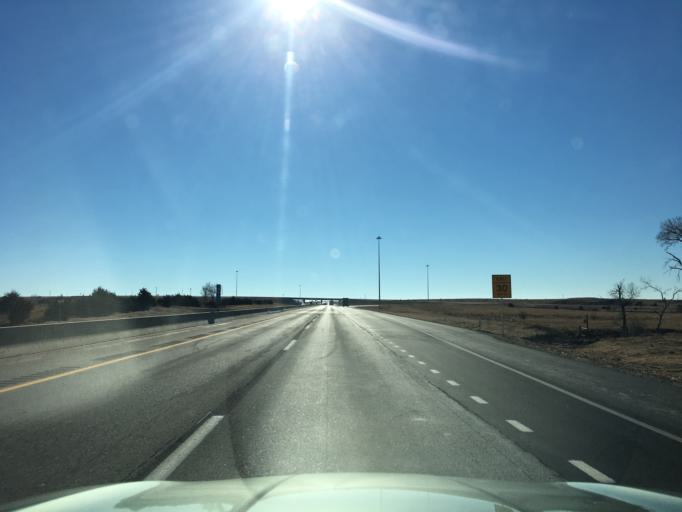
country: US
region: Kansas
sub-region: Sumner County
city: Wellington
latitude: 37.0628
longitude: -97.3385
